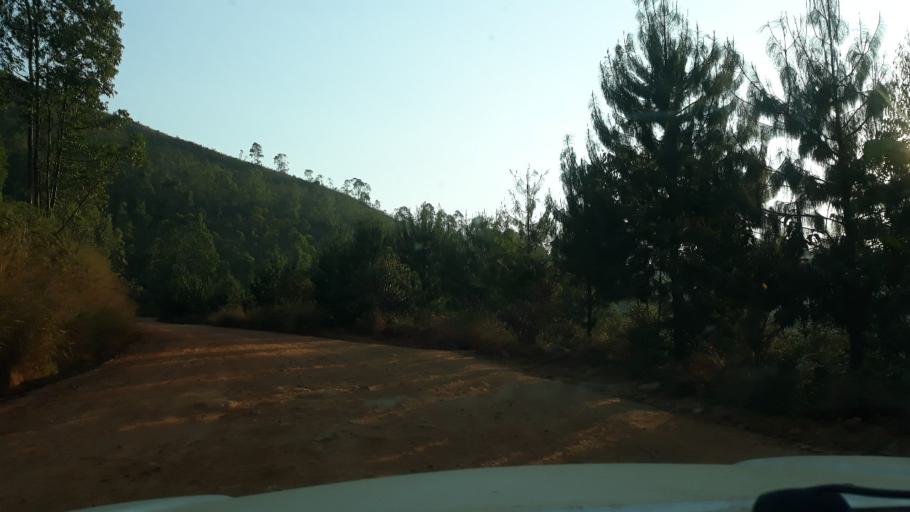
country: RW
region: Western Province
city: Cyangugu
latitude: -2.6983
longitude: 28.9049
